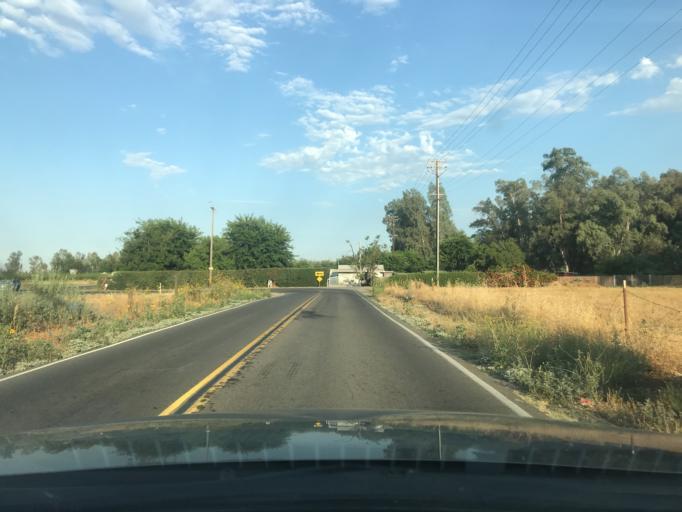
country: US
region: California
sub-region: Merced County
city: Atwater
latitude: 37.3494
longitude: -120.5578
